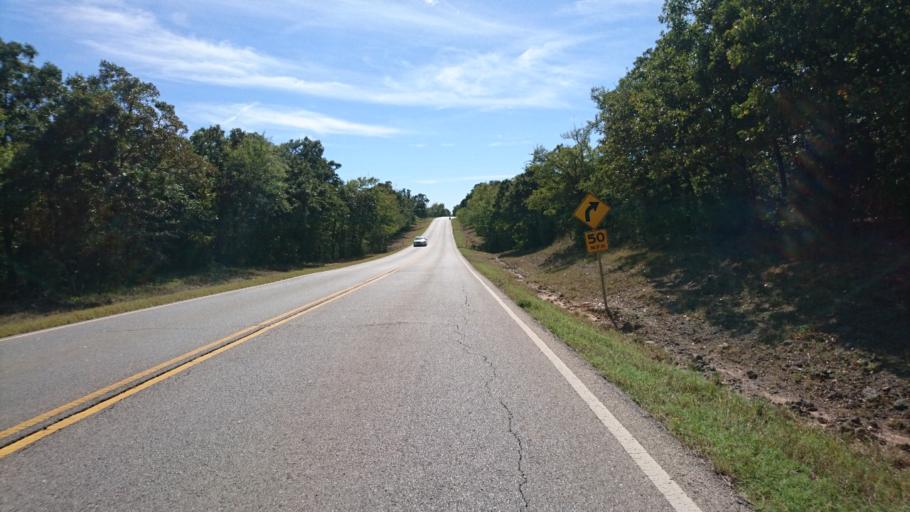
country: US
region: Oklahoma
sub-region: Lincoln County
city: Stroud
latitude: 35.7270
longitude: -96.7288
